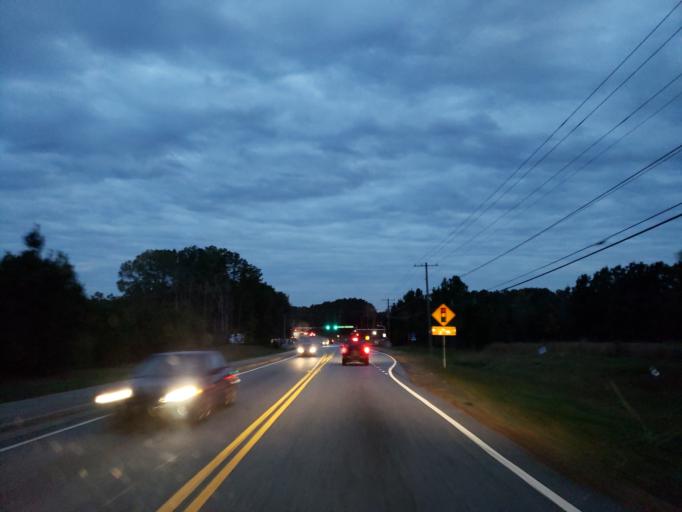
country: US
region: Georgia
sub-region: Cobb County
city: Powder Springs
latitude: 33.9347
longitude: -84.7002
